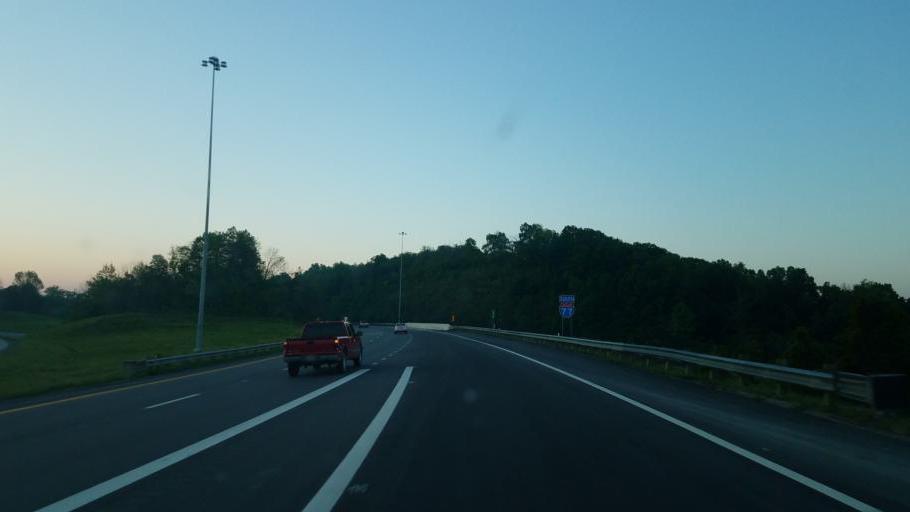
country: US
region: Ohio
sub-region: Guernsey County
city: Byesville
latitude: 39.9979
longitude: -81.5604
